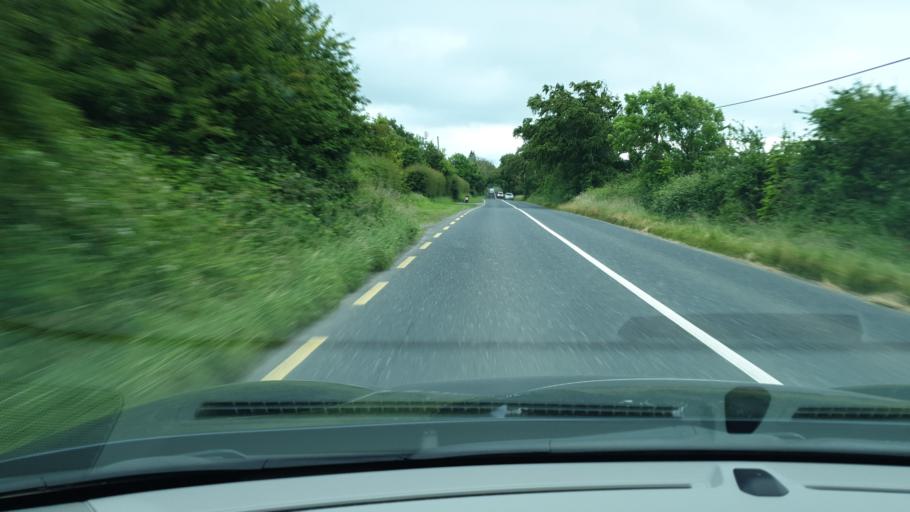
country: IE
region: Leinster
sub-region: An Mhi
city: Dunshaughlin
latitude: 53.4651
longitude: -6.5289
